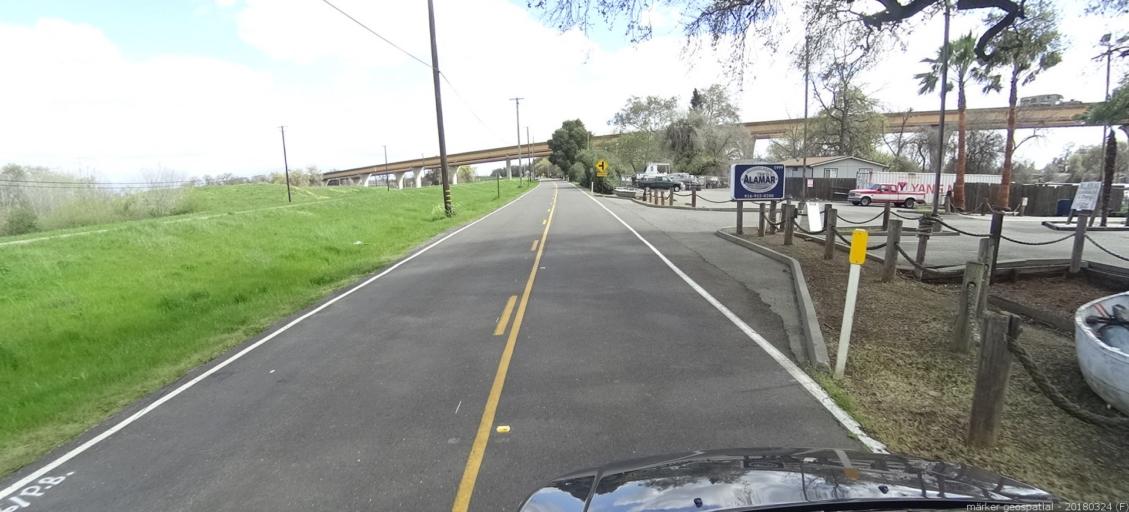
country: US
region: California
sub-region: Yolo County
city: West Sacramento
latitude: 38.6753
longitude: -121.6265
